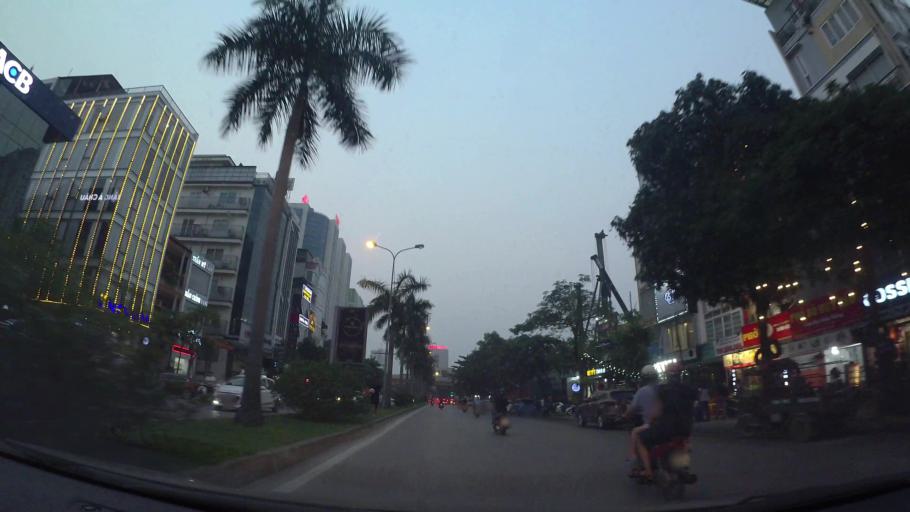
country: VN
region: Ha Noi
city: Ha Dong
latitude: 20.9778
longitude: 105.7877
